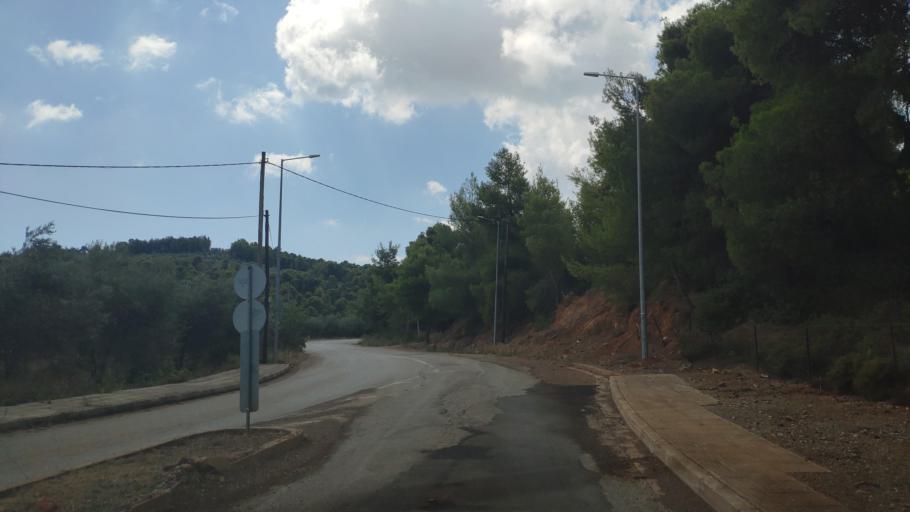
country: GR
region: Central Greece
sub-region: Nomos Fthiotidos
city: Malesina
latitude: 38.6451
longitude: 23.2004
